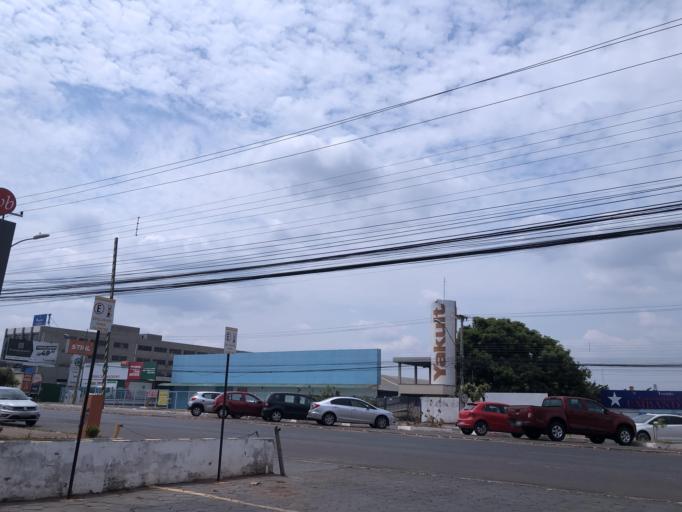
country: BR
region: Federal District
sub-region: Brasilia
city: Brasilia
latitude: -15.8031
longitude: -47.9637
